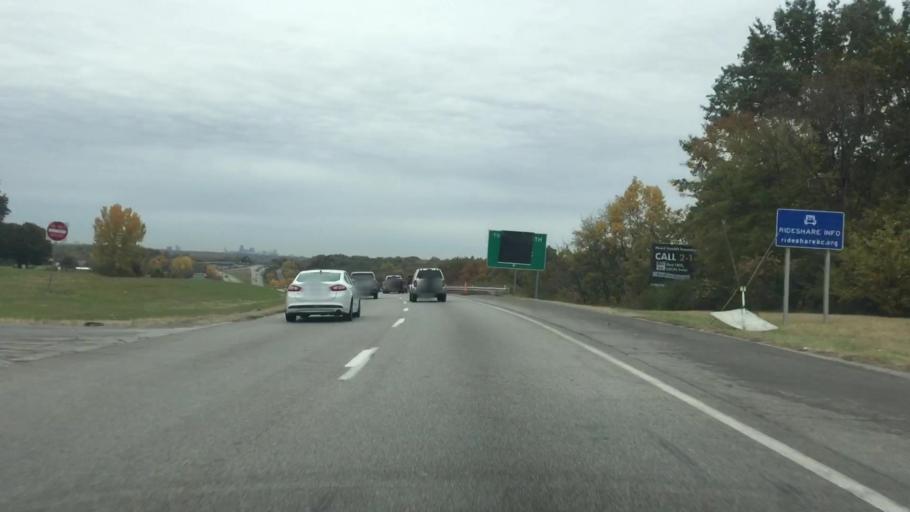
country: US
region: Missouri
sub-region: Jackson County
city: Raytown
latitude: 39.0062
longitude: -94.4853
